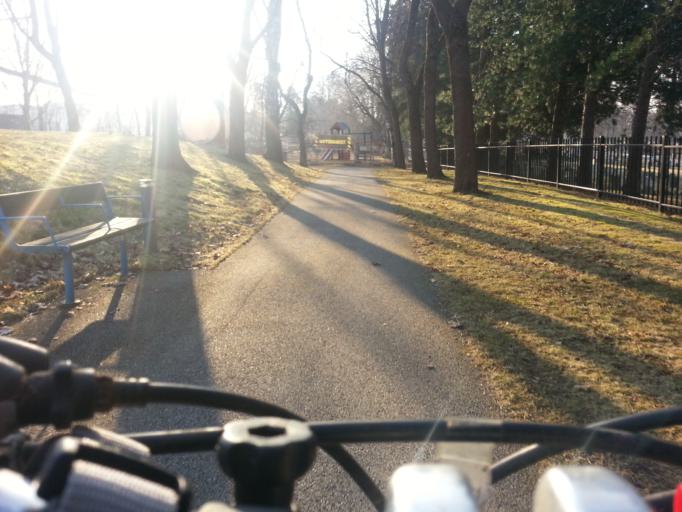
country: NO
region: Sor-Trondelag
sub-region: Trondheim
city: Trondheim
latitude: 63.4184
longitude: 10.3888
